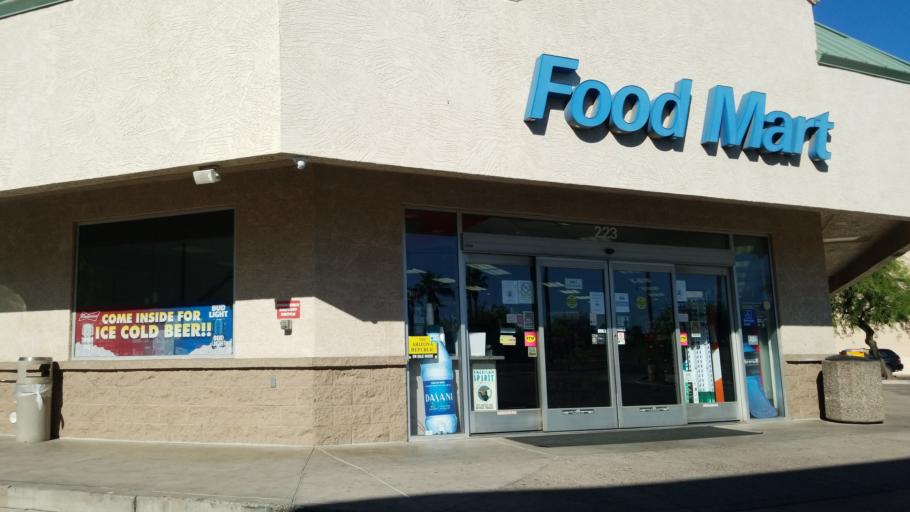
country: US
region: Arizona
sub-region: Maricopa County
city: Phoenix
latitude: 33.4944
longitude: -112.0700
